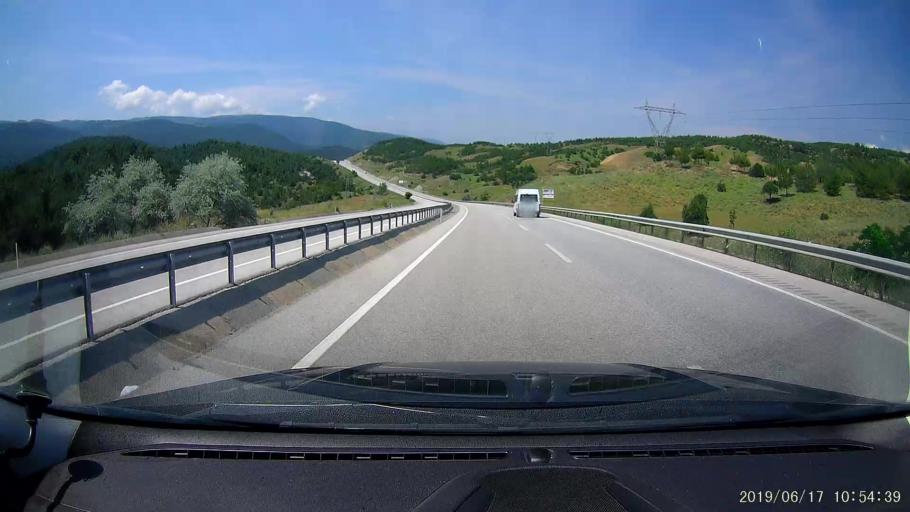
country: TR
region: Corum
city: Hacihamza
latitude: 41.0686
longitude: 34.2958
